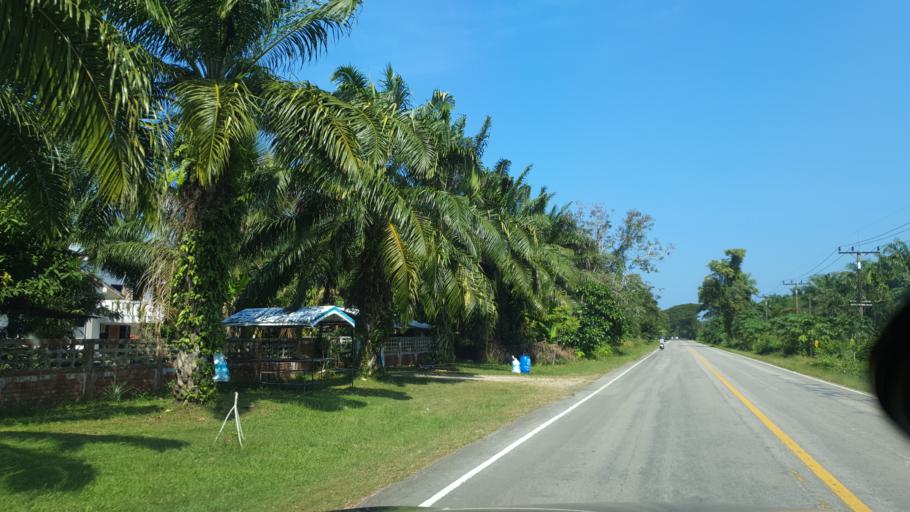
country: TH
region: Surat Thani
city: Tha Chana
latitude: 9.5802
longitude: 99.1914
